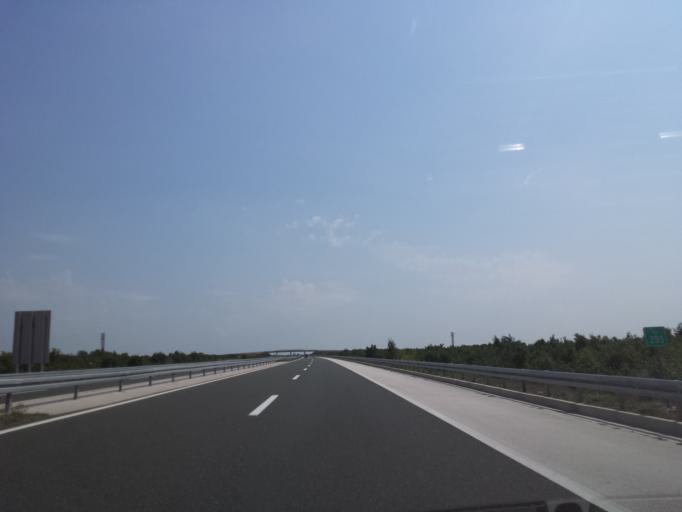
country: HR
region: Sibensko-Kniniska
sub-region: Grad Sibenik
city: Pirovac
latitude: 43.9309
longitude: 15.7151
